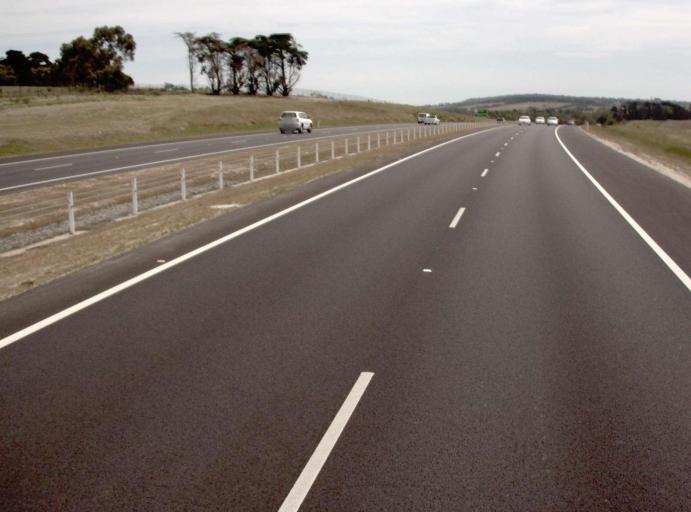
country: AU
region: Victoria
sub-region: Mornington Peninsula
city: Moorooduc
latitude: -38.2700
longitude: 145.0913
